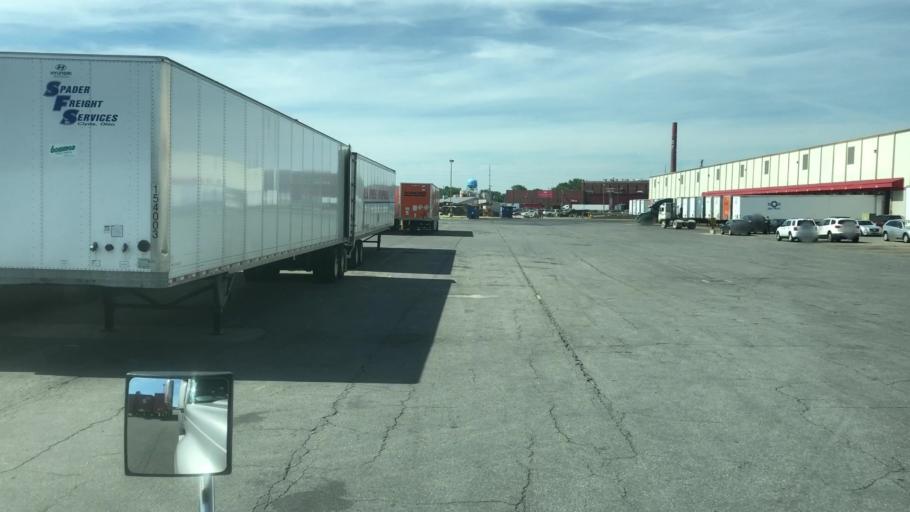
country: US
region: Ohio
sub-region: Sandusky County
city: Fremont
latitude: 41.3632
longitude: -83.0899
